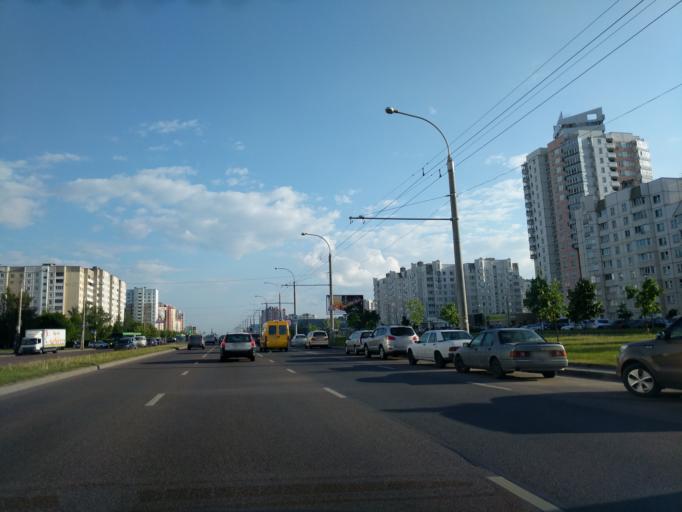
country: BY
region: Minsk
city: Zhdanovichy
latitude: 53.9129
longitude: 27.4364
